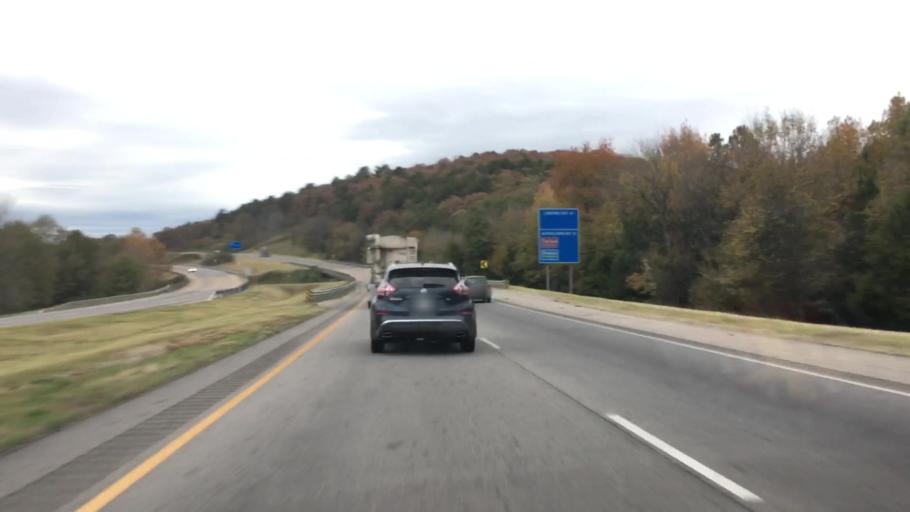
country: US
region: Arkansas
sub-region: Johnson County
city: Coal Hill
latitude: 35.5024
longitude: -93.7279
